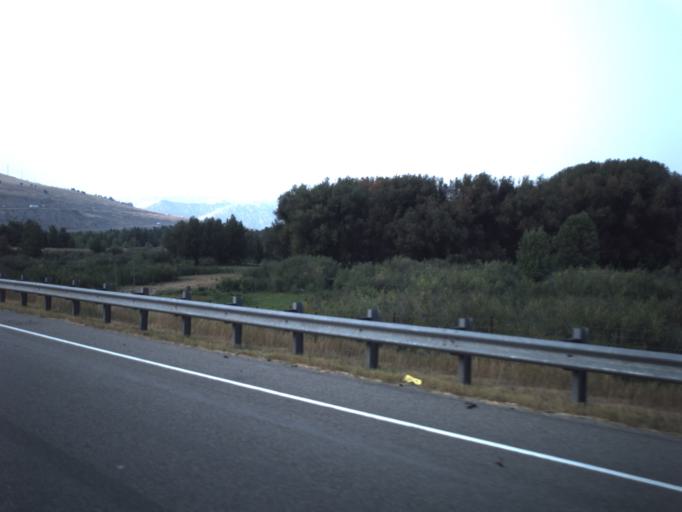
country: US
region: Utah
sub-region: Summit County
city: Coalville
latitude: 40.9168
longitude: -111.4061
